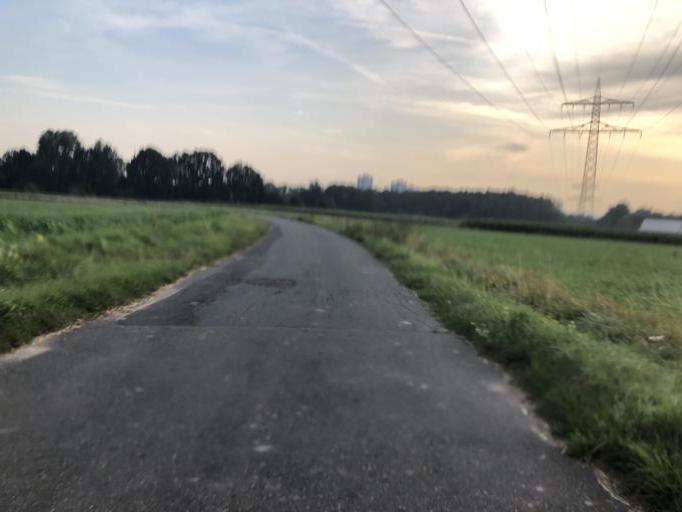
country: DE
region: Bavaria
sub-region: Regierungsbezirk Mittelfranken
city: Erlangen
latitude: 49.5845
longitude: 10.9586
